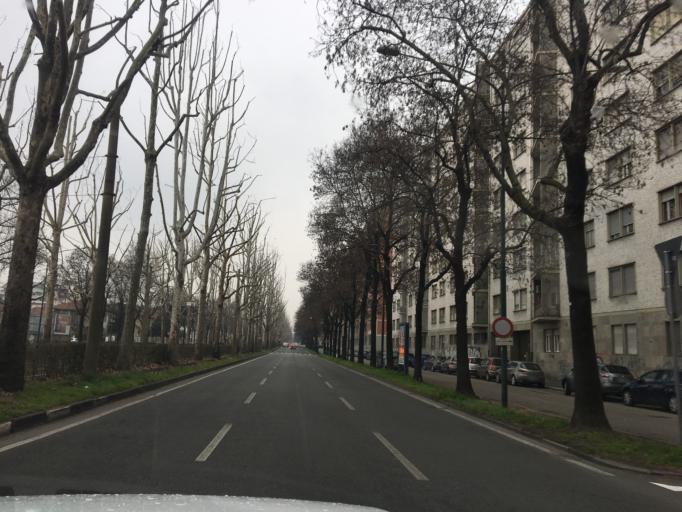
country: IT
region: Piedmont
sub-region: Provincia di Torino
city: Lesna
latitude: 45.0340
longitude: 7.6424
